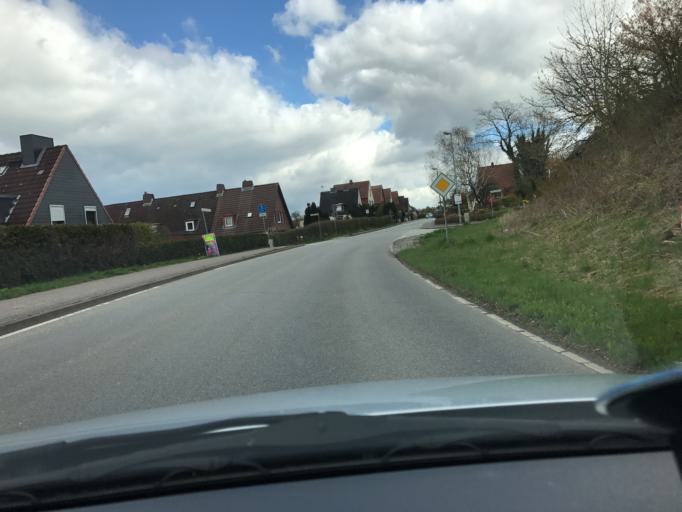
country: DE
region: Schleswig-Holstein
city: Eutin
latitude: 54.1257
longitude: 10.6039
